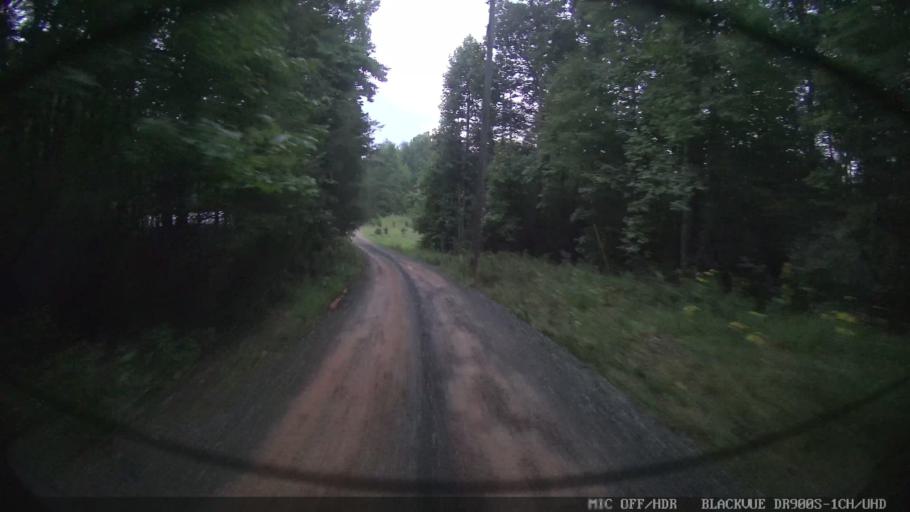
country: US
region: Georgia
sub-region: Gilmer County
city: Ellijay
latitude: 34.6978
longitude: -84.3297
